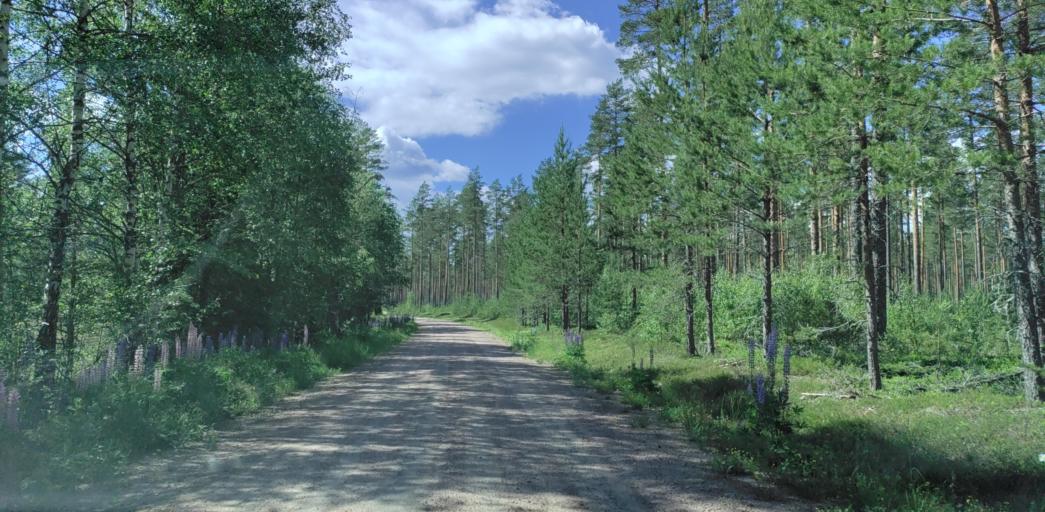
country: SE
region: Vaermland
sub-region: Munkfors Kommun
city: Munkfors
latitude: 59.9611
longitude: 13.5095
